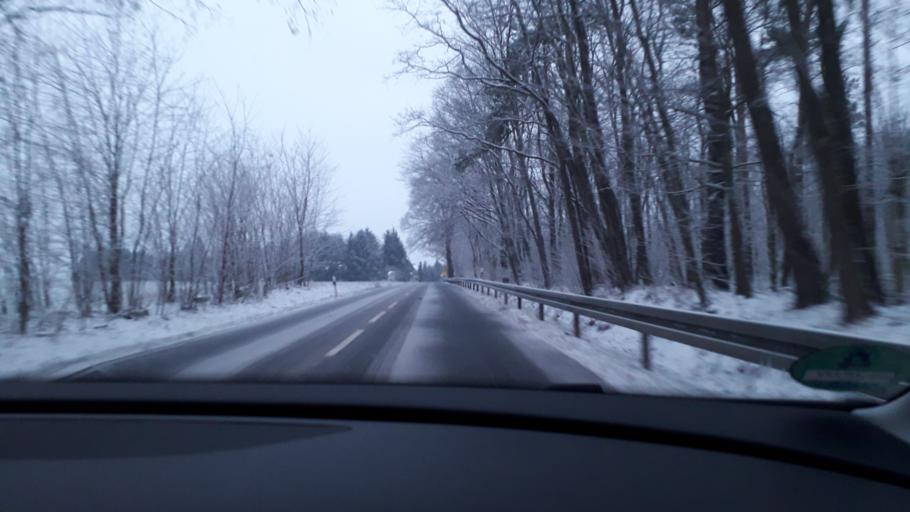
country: DE
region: Brandenburg
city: Spremberg
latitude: 51.5998
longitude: 14.4545
